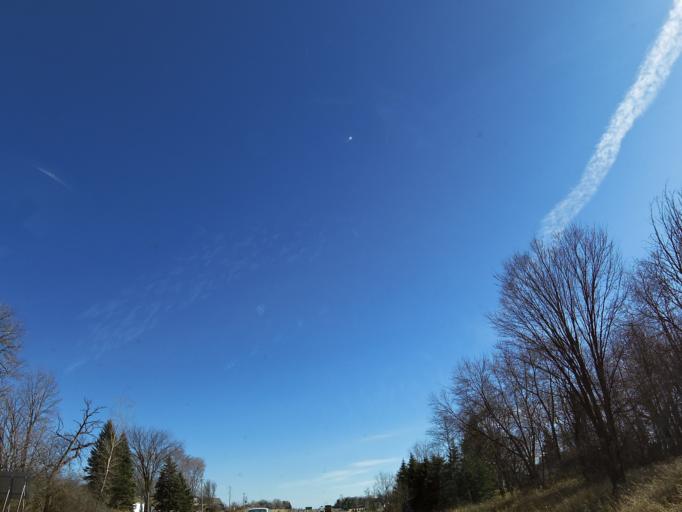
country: US
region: Minnesota
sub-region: Hennepin County
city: Corcoran
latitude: 45.0412
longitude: -93.5207
